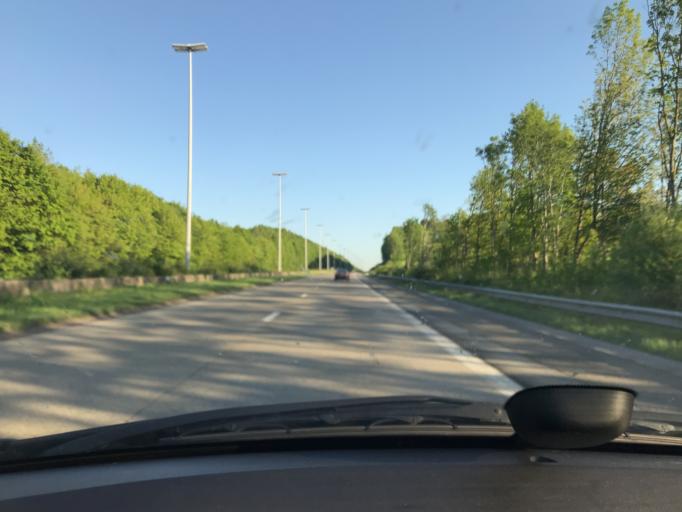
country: BE
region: Wallonia
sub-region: Province de Namur
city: Assesse
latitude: 50.3613
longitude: 5.0032
